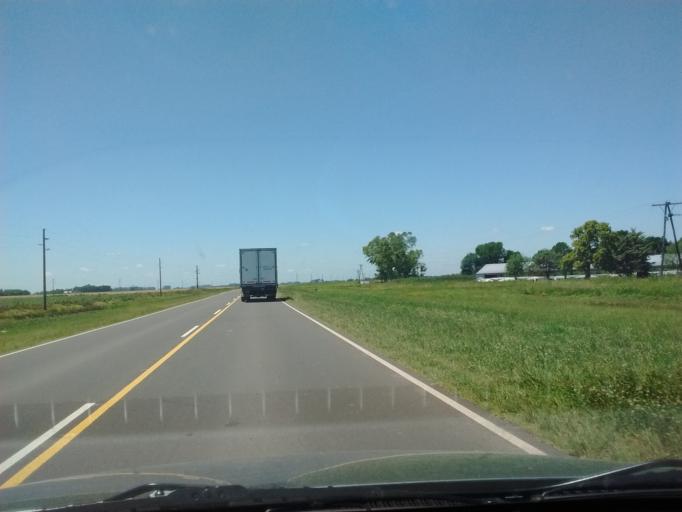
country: AR
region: Entre Rios
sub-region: Departamento de Gualeguay
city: Gualeguay
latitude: -33.0407
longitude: -59.4312
